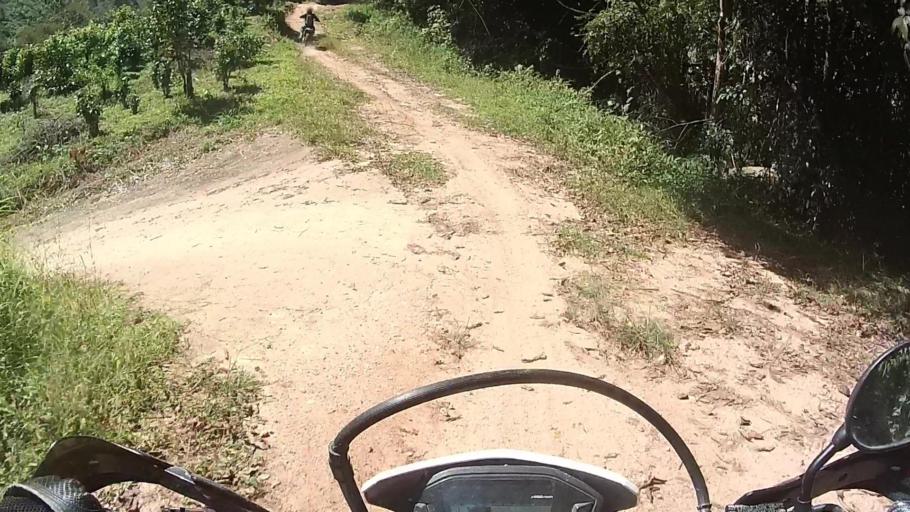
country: TH
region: Chiang Mai
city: Phrao
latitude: 19.4651
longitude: 99.3182
